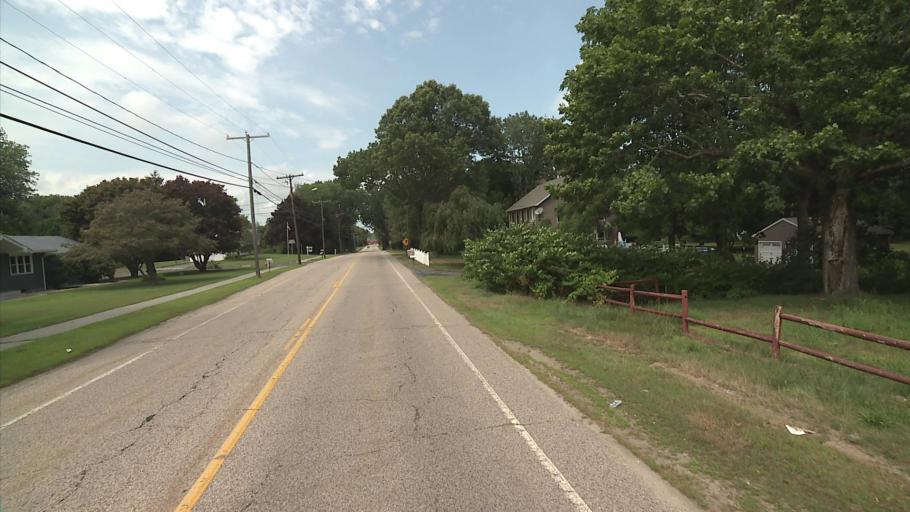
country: US
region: Connecticut
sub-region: New London County
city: Central Waterford
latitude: 41.3266
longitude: -72.1345
